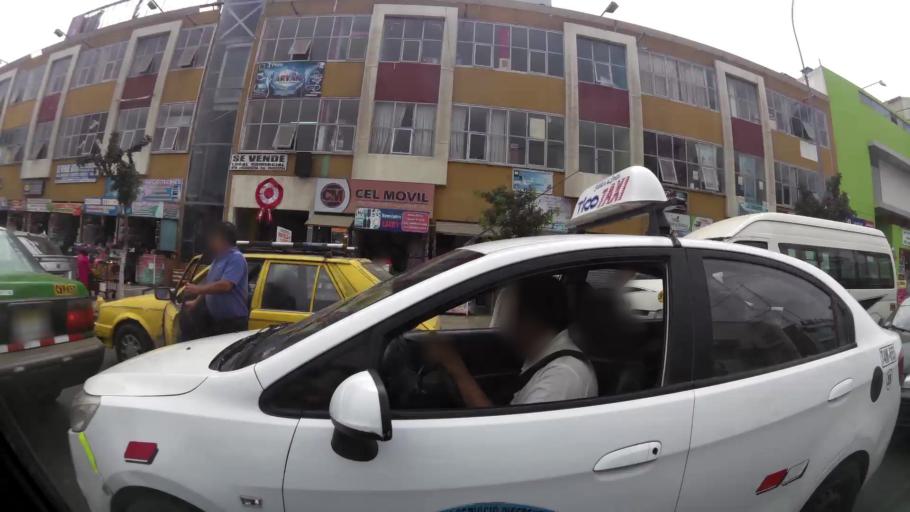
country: PE
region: La Libertad
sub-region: Provincia de Trujillo
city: Trujillo
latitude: -8.1156
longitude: -79.0254
